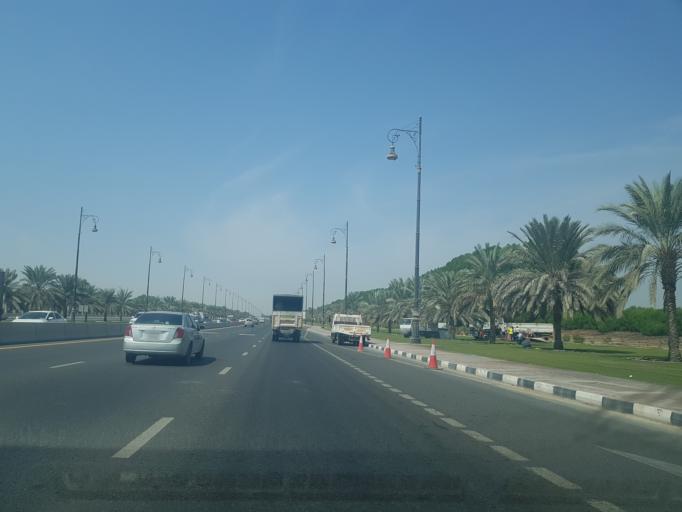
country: AE
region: Ash Shariqah
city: Sharjah
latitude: 25.3144
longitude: 55.5406
